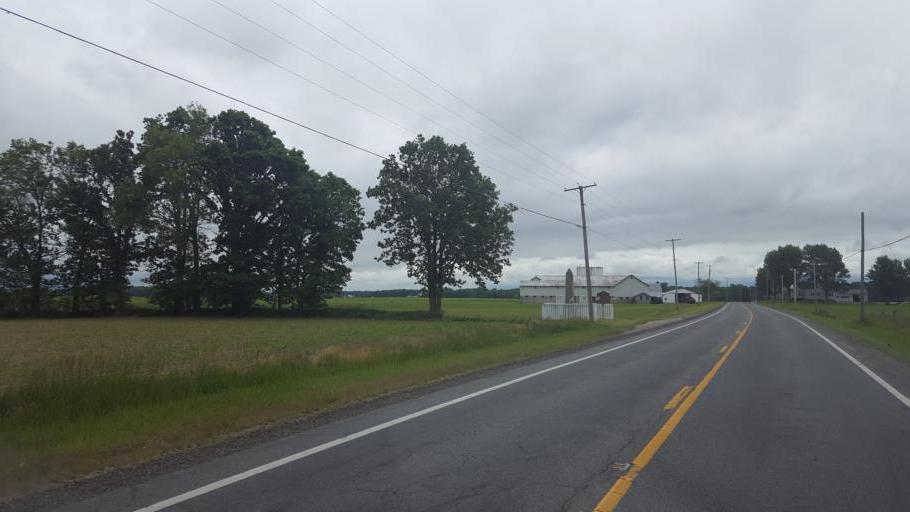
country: US
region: Ohio
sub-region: Crawford County
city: Bucyrus
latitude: 40.7705
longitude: -82.8973
